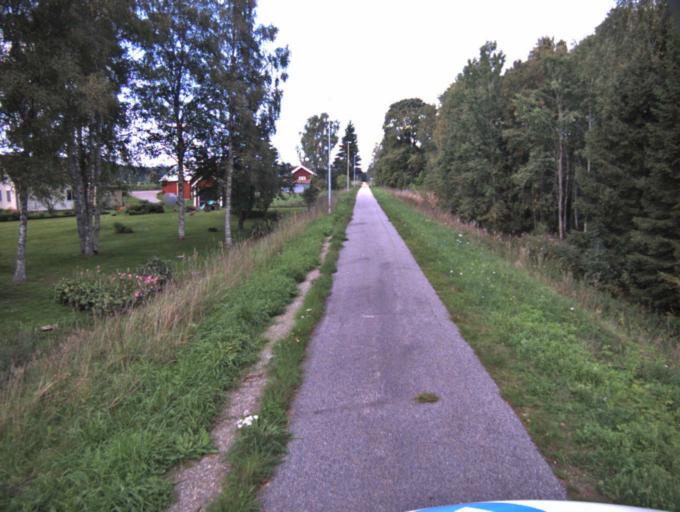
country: SE
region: Vaestra Goetaland
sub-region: Ulricehamns Kommun
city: Ulricehamn
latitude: 57.8663
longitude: 13.4292
